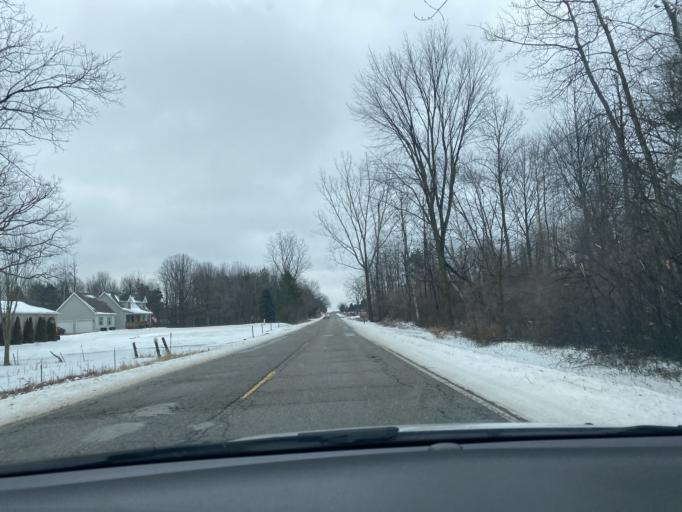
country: US
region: Michigan
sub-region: Lapeer County
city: North Branch
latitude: 43.2066
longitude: -83.2420
